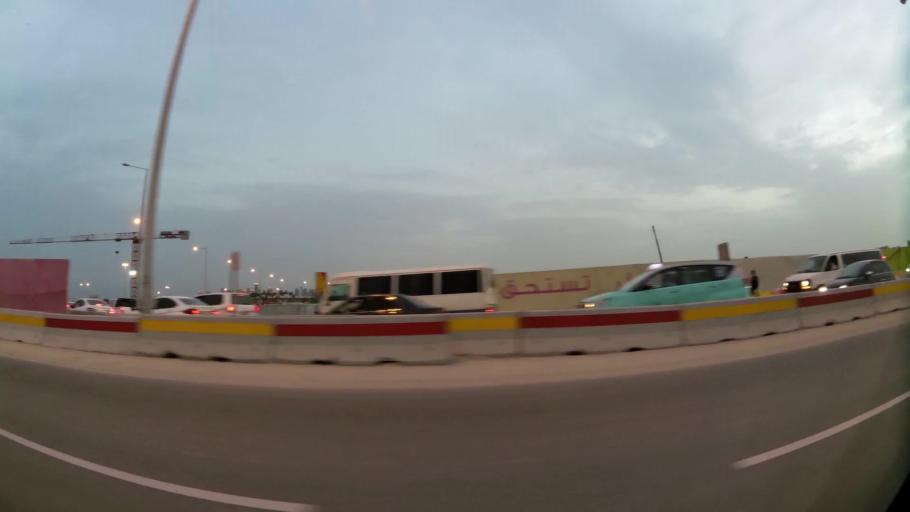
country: QA
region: Baladiyat ad Dawhah
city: Doha
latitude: 25.3717
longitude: 51.5239
